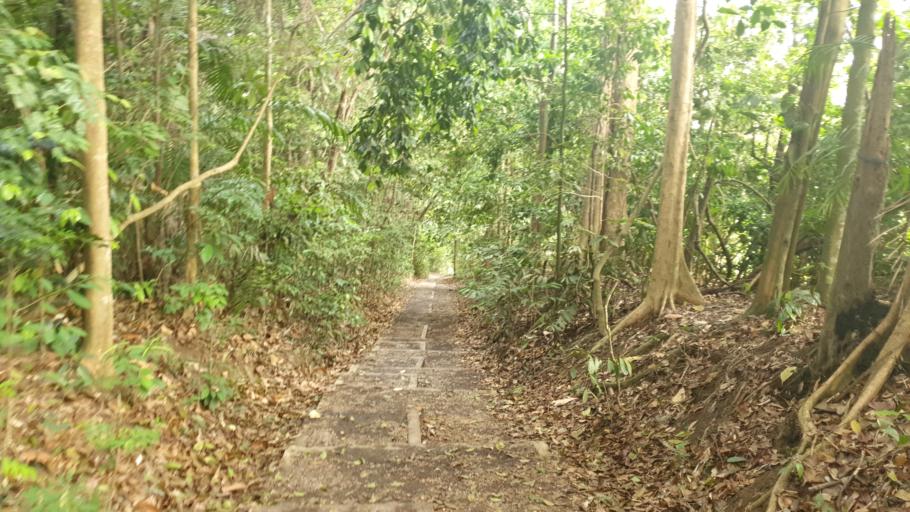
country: SG
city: Singapore
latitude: 1.3390
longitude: 103.8165
